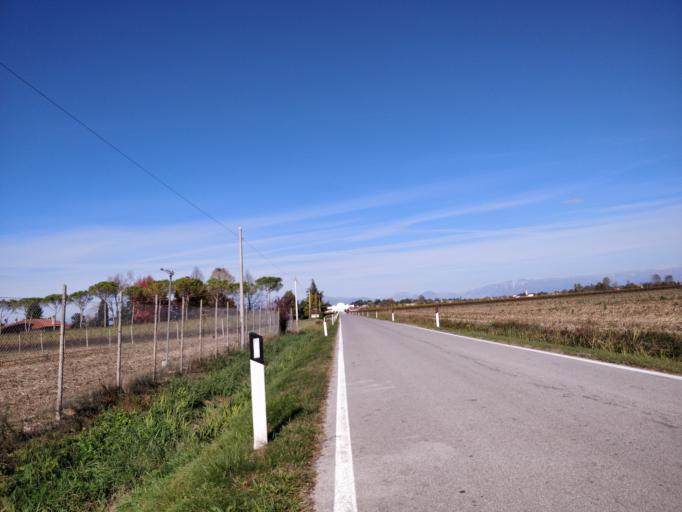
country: IT
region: Friuli Venezia Giulia
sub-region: Provincia di Udine
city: Codroipo
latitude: 45.9359
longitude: 13.0112
